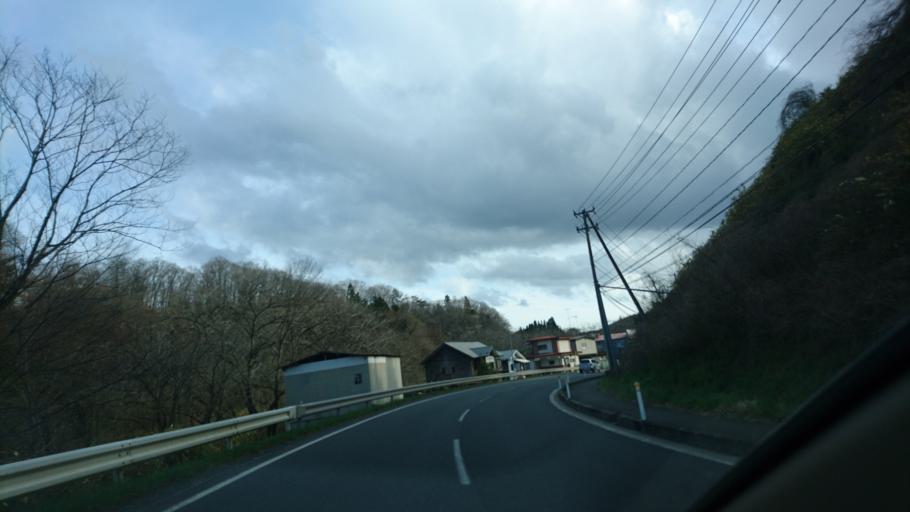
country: JP
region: Iwate
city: Ichinoseki
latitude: 38.9304
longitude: 141.3409
